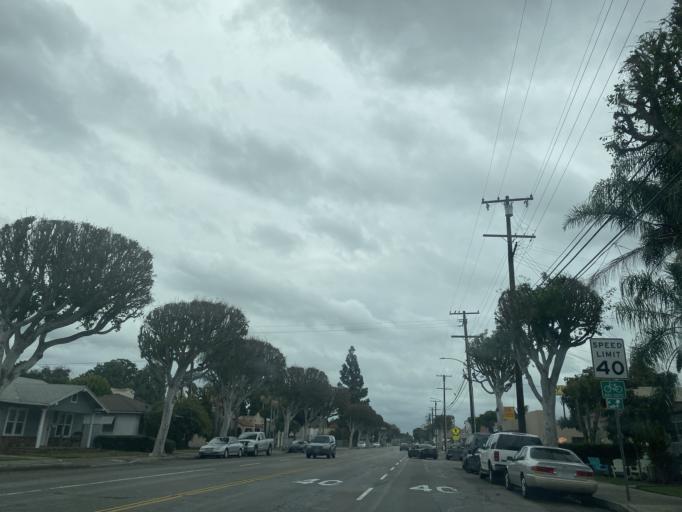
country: US
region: California
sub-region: Orange County
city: Fullerton
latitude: 33.8704
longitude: -117.9141
